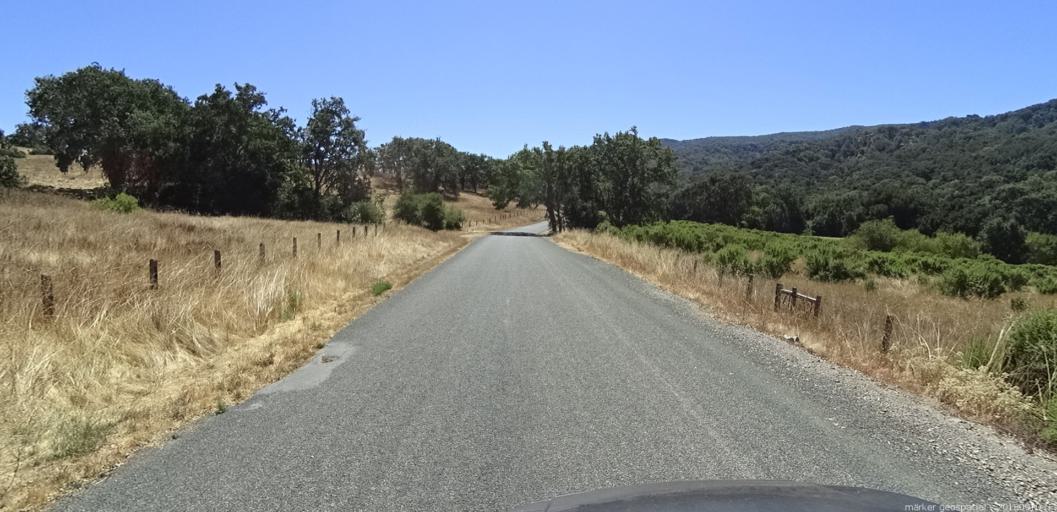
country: US
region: California
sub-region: Monterey County
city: Carmel Valley Village
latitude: 36.4521
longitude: -121.7973
